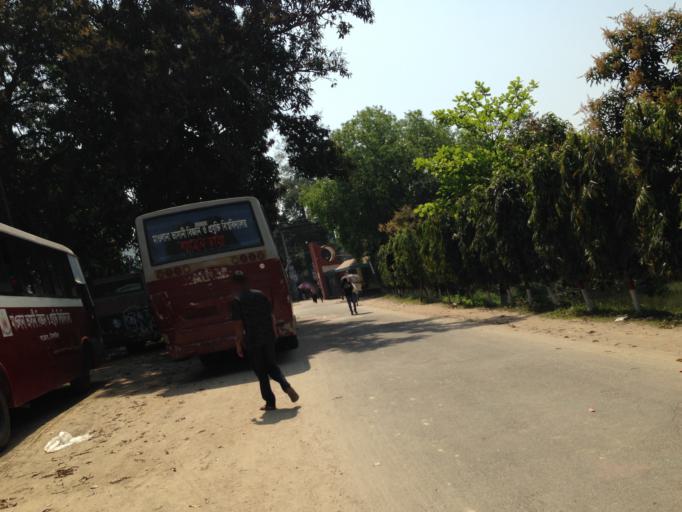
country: BD
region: Dhaka
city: Tangail
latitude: 24.2344
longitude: 89.8924
